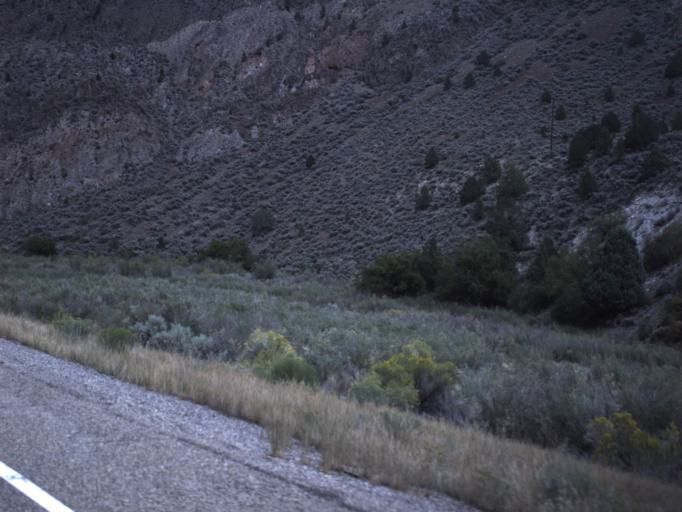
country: US
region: Utah
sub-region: Piute County
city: Junction
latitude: 38.0996
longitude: -112.3360
